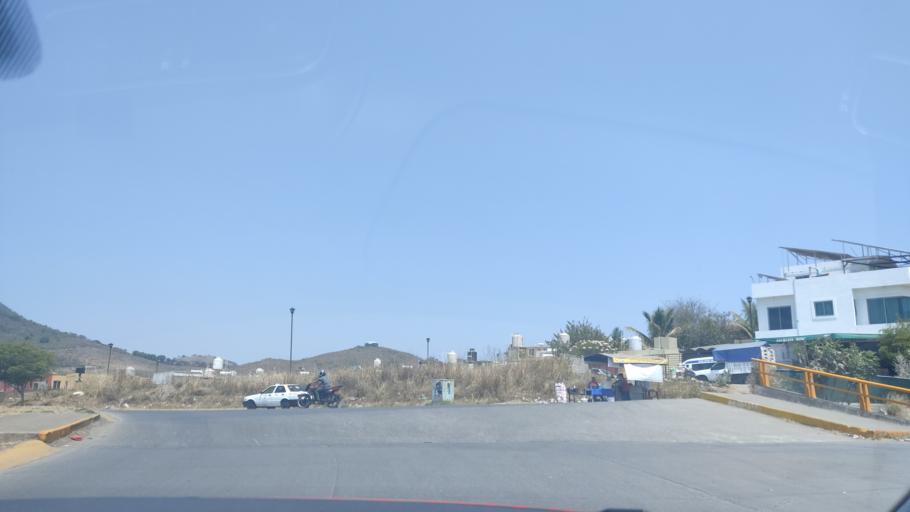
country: MX
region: Nayarit
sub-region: Tepic
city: La Corregidora
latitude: 21.4939
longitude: -104.8208
